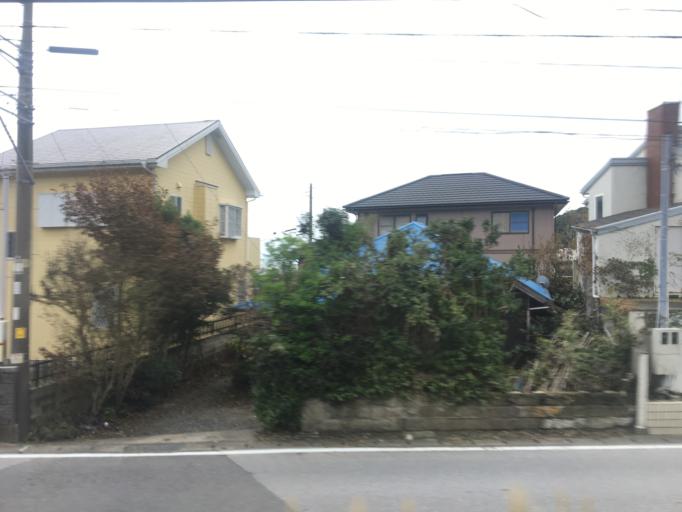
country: JP
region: Chiba
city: Katsuura
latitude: 35.1386
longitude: 140.2577
